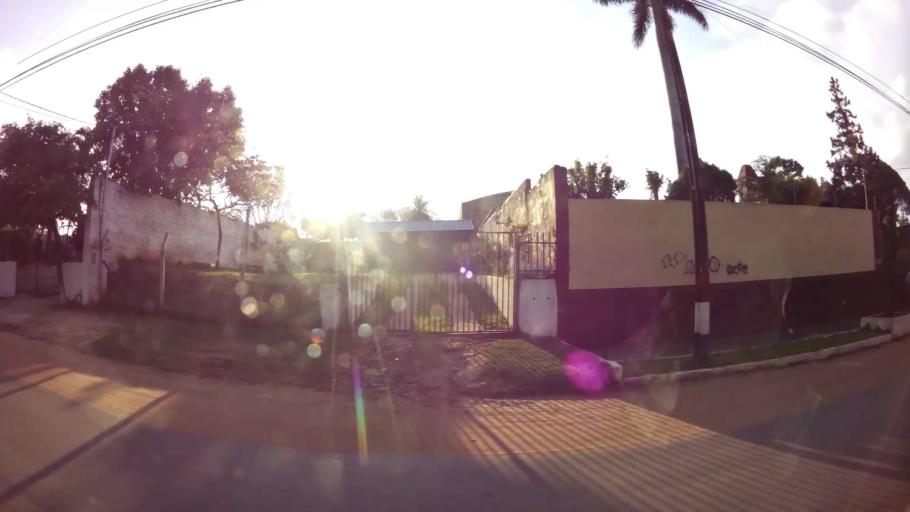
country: PY
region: Central
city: Fernando de la Mora
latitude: -25.3532
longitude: -57.5279
